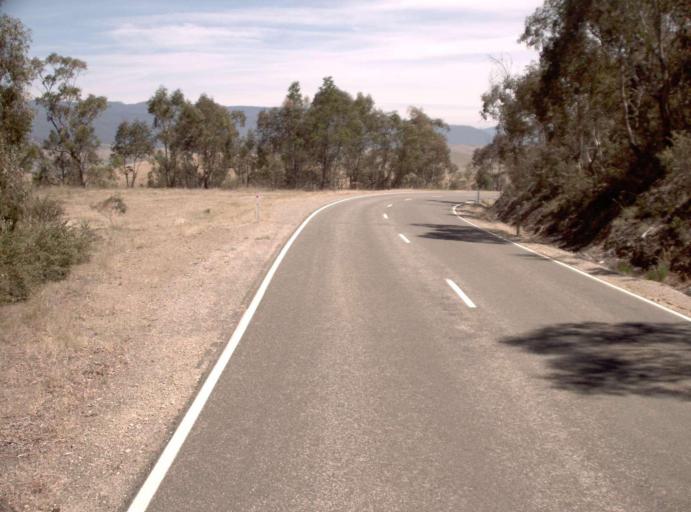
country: AU
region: Victoria
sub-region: Alpine
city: Mount Beauty
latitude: -37.0351
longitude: 147.6431
